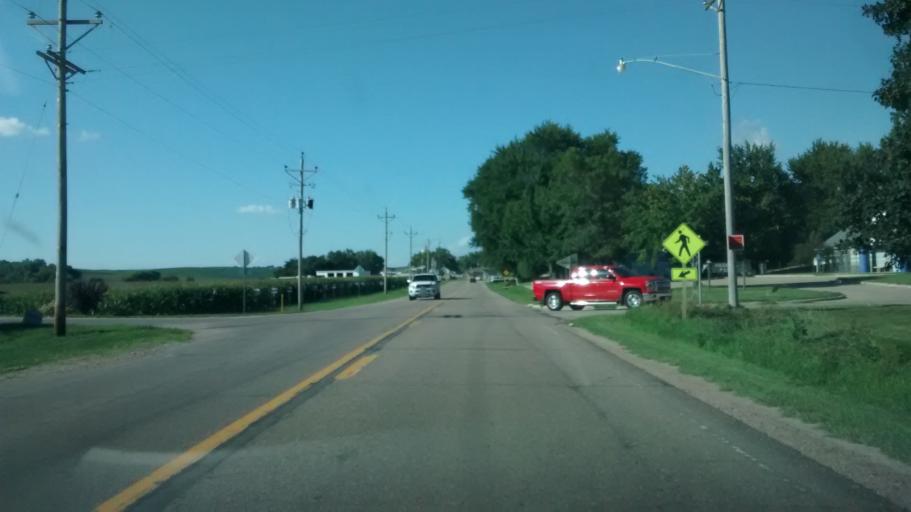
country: US
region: Iowa
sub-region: Woodbury County
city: Moville
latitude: 42.4838
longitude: -96.0757
